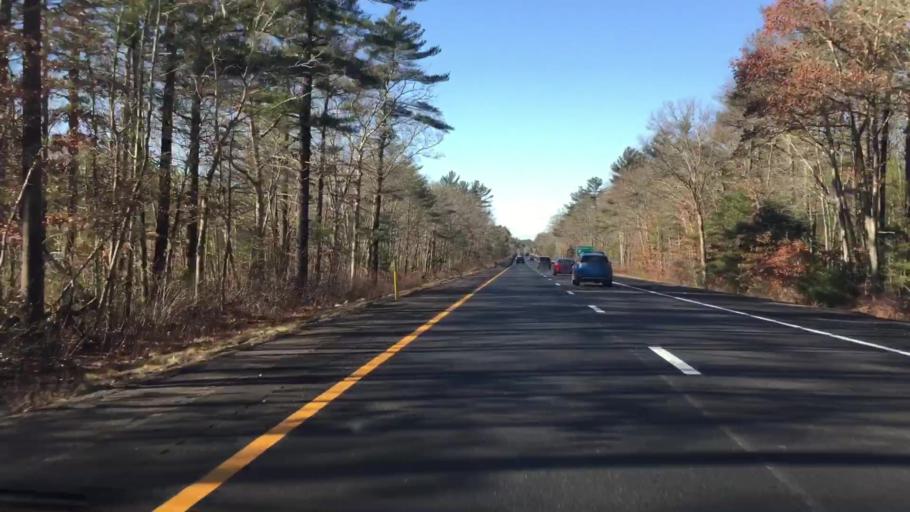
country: US
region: Massachusetts
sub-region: Plymouth County
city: West Wareham
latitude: 41.8098
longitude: -70.7794
